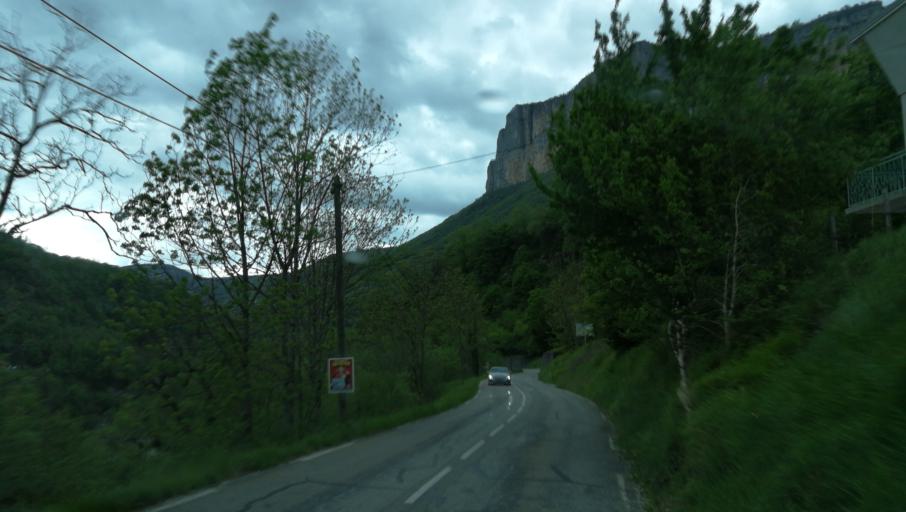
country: FR
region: Rhone-Alpes
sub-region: Departement de l'Isere
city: Pont-en-Royans
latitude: 45.0646
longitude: 5.3983
